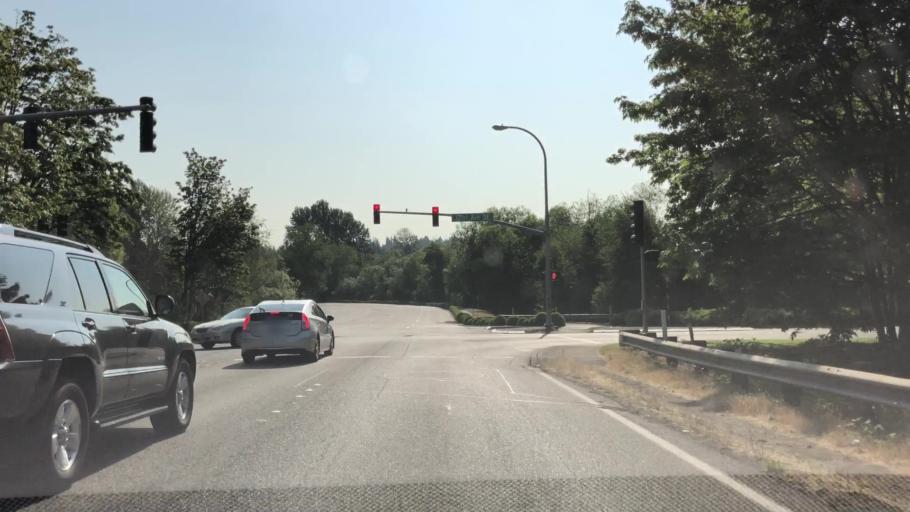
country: US
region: Washington
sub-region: King County
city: Bellevue
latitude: 47.6033
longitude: -122.1808
